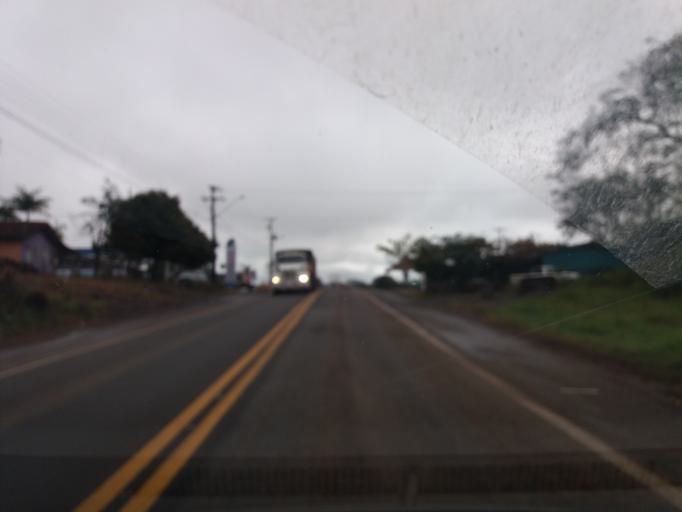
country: BR
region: Parana
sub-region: Cascavel
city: Cascavel
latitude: -25.2854
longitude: -53.5689
